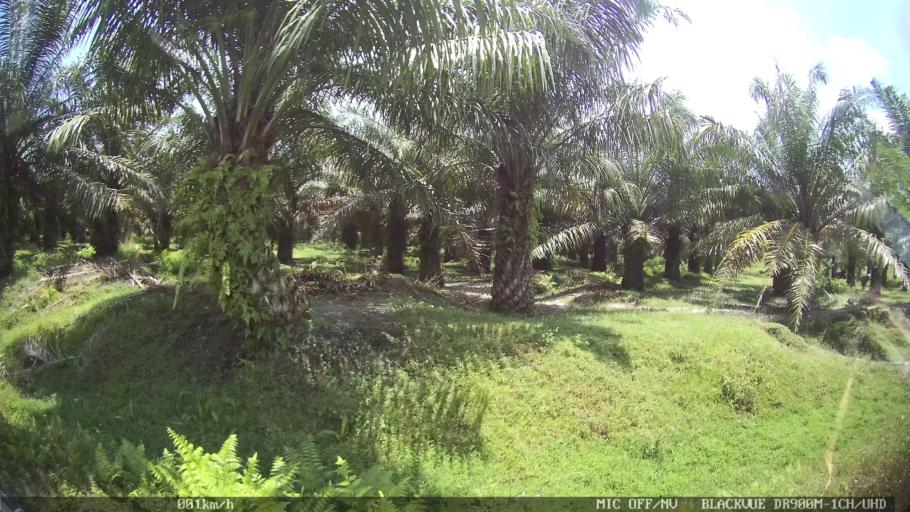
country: ID
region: North Sumatra
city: Percut
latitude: 3.5355
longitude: 98.8653
